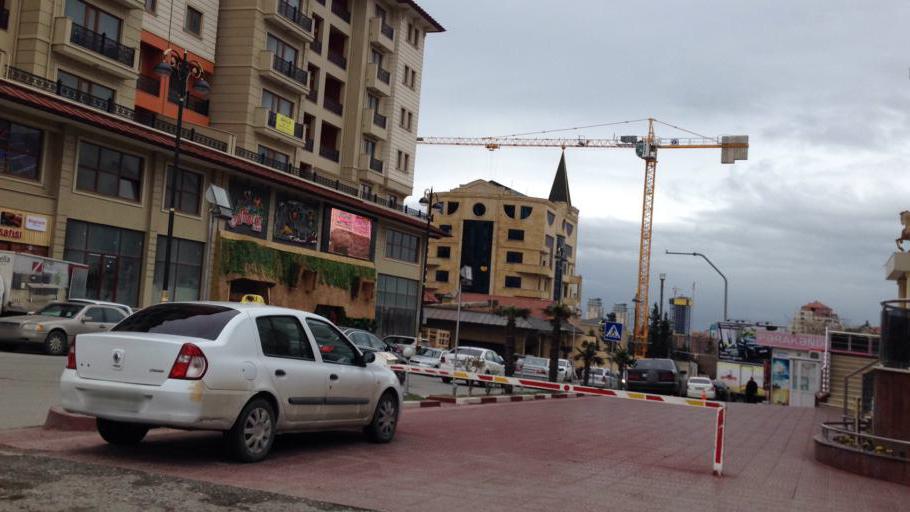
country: AZ
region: Baki
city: Baku
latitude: 40.3911
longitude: 49.8491
